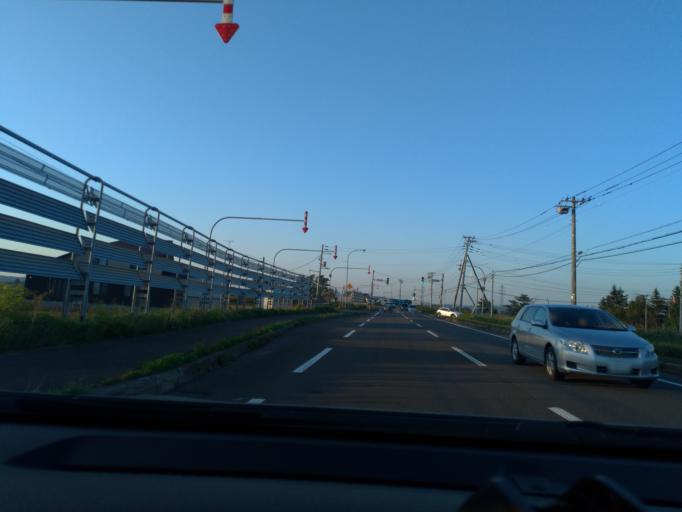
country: JP
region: Hokkaido
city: Tobetsu
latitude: 43.1892
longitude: 141.5245
